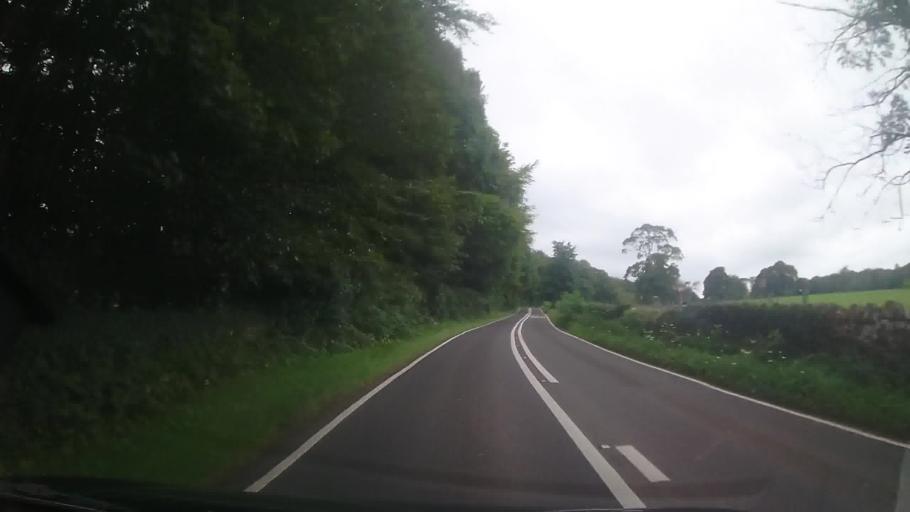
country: GB
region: Wales
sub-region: Gwynedd
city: Y Felinheli
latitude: 53.2028
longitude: -4.2231
